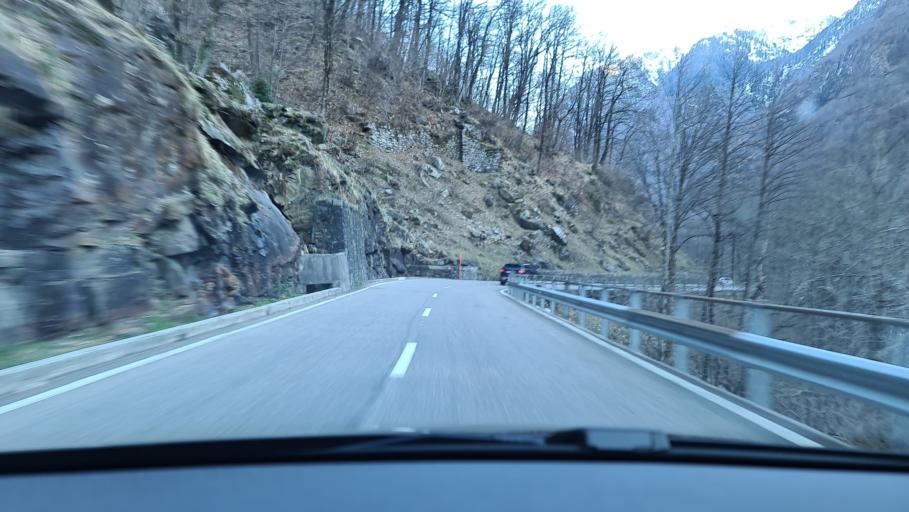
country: CH
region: Ticino
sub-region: Locarno District
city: Lavertezzo
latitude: 46.2846
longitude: 8.8018
